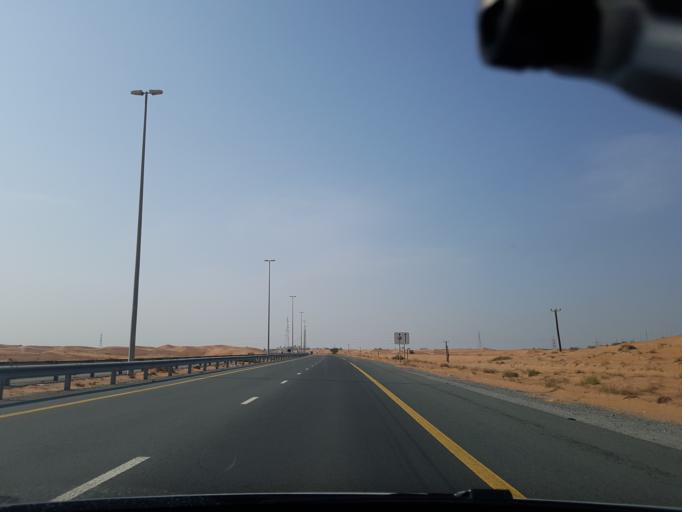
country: AE
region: Umm al Qaywayn
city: Umm al Qaywayn
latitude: 25.5220
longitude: 55.7375
